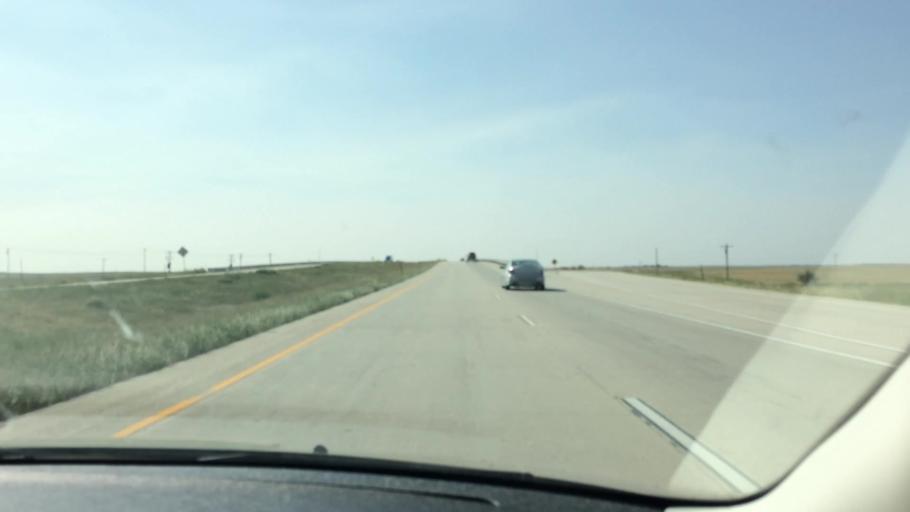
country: US
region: Colorado
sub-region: Arapahoe County
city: Byers
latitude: 39.6802
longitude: -104.1122
